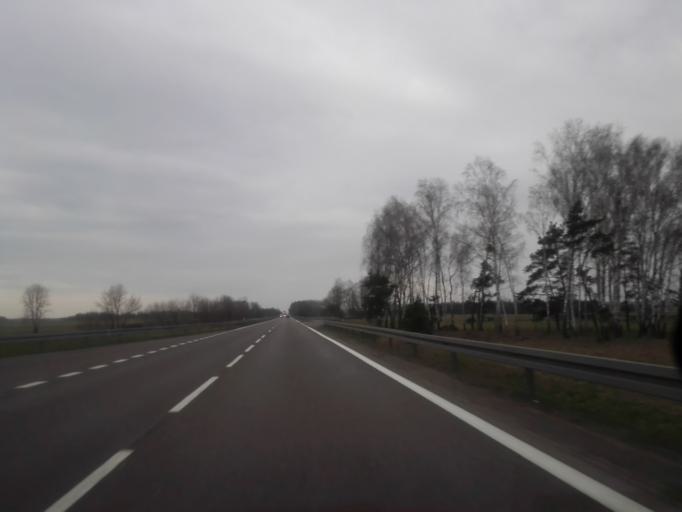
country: PL
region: Podlasie
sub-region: Powiat grajewski
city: Rajgrod
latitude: 53.6805
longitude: 22.6072
